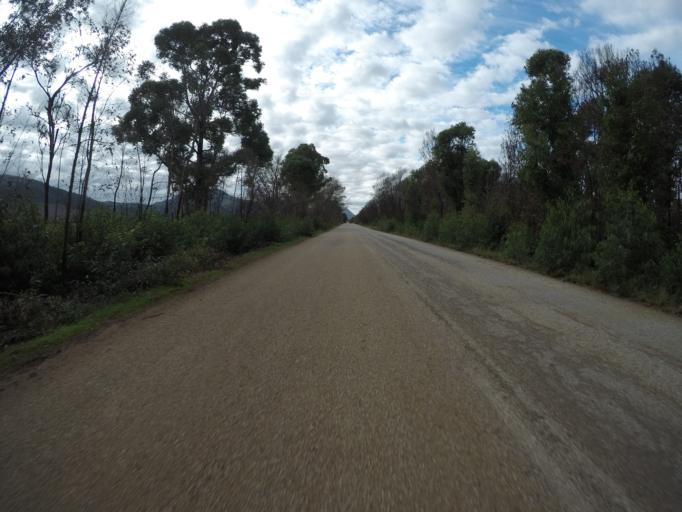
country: ZA
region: Eastern Cape
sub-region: Cacadu District Municipality
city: Kareedouw
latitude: -34.0148
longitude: 24.3200
